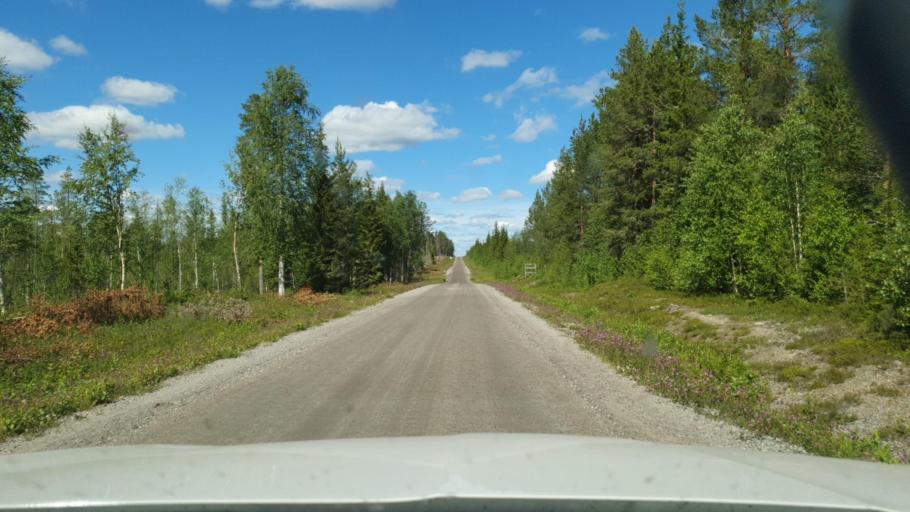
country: SE
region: Vaesterbotten
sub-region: Skelleftea Kommun
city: Byske
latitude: 65.1289
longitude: 21.2010
